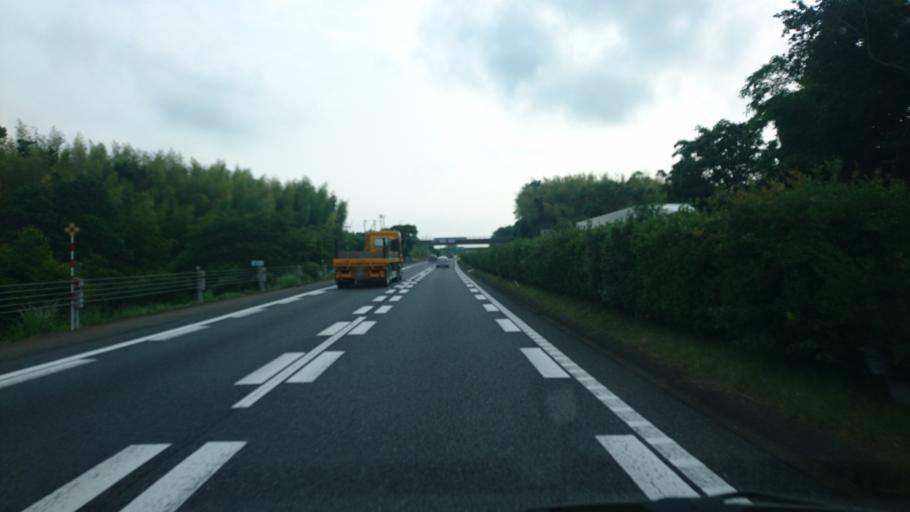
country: JP
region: Chiba
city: Narita
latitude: 35.8054
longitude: 140.3688
